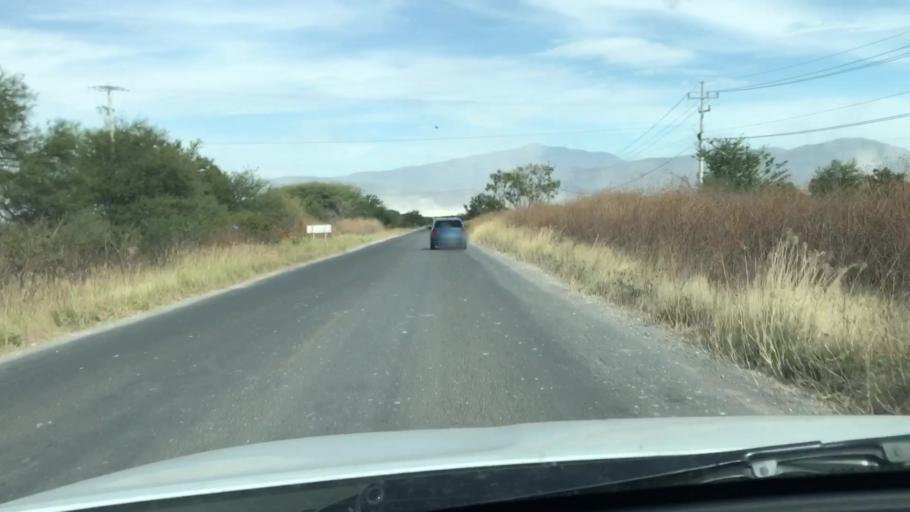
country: MX
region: Jalisco
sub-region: Zacoalco de Torres
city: Barranca de Otates (Barranca de Otatan)
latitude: 20.2786
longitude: -103.6253
